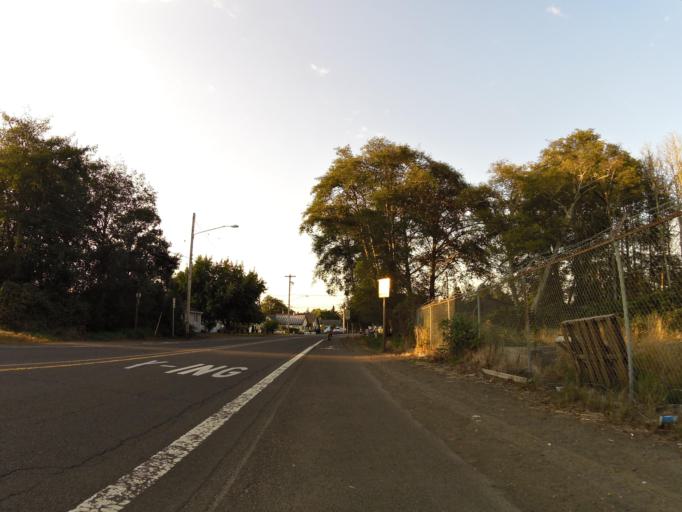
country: US
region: Oregon
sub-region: Clatsop County
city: Warrenton
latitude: 46.1566
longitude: -123.9279
